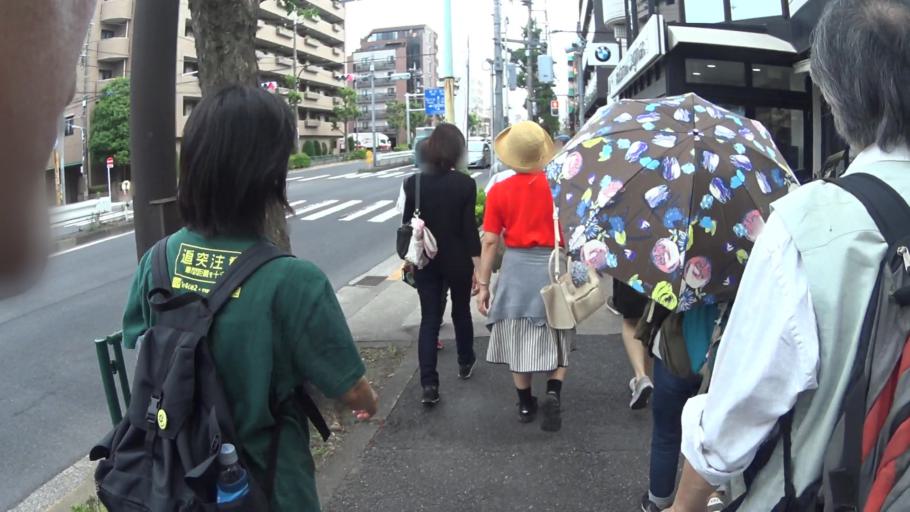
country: JP
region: Tokyo
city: Musashino
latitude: 35.7138
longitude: 139.6144
